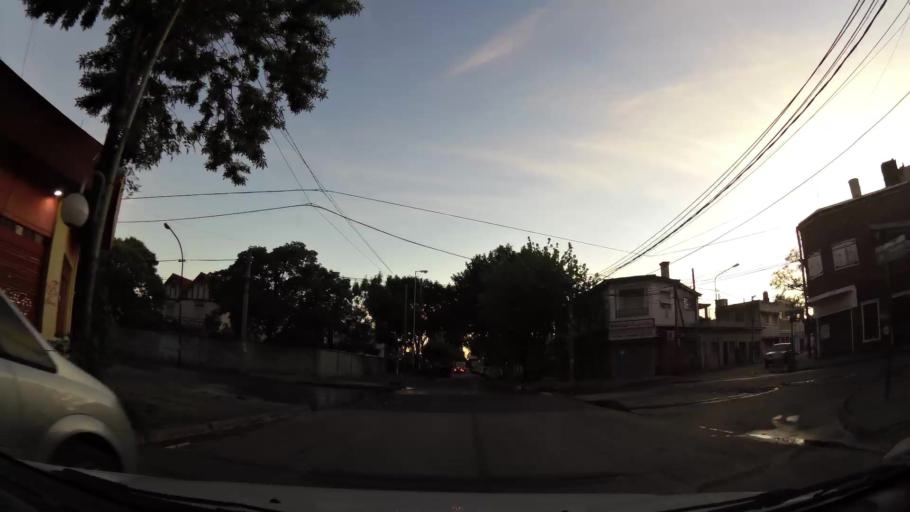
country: AR
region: Buenos Aires
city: Ituzaingo
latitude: -34.6550
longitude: -58.6433
